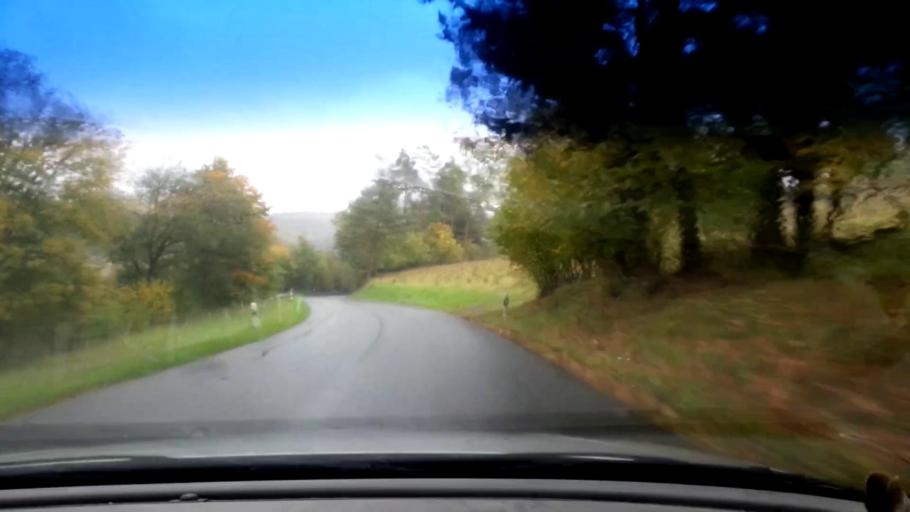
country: DE
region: Bavaria
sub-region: Upper Franconia
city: Stadelhofen
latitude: 50.0267
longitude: 11.1916
